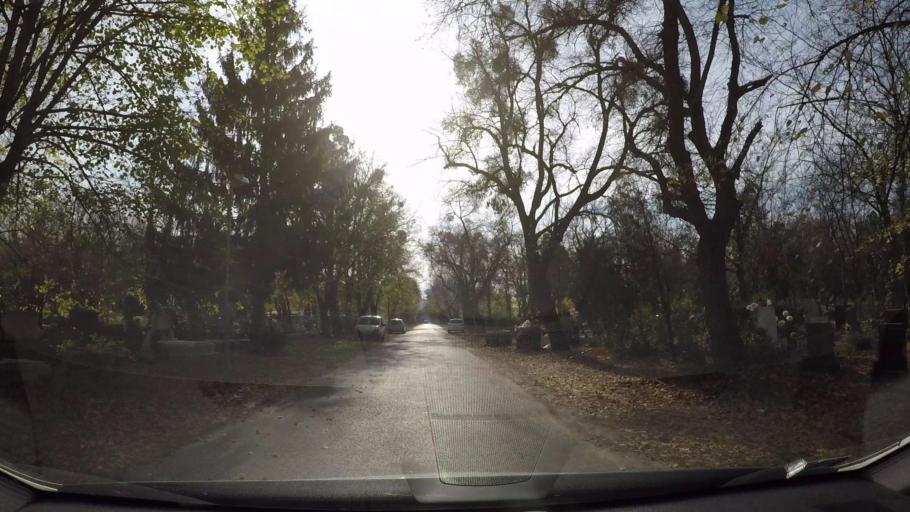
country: HU
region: Budapest
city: Budapest X. keruelet
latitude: 47.4754
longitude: 19.1799
